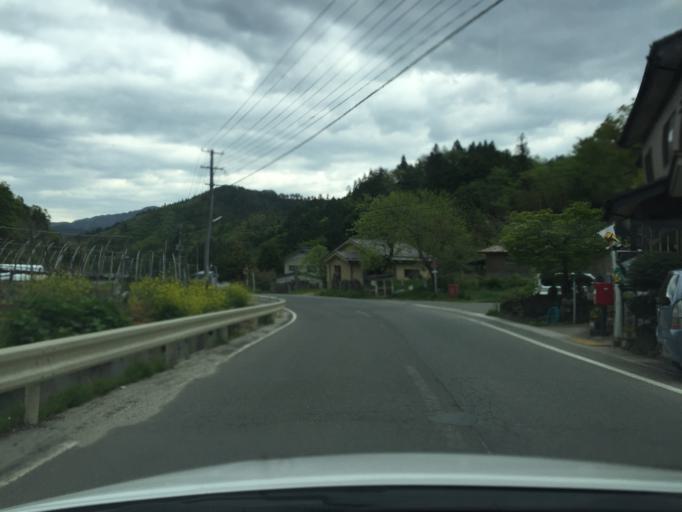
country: JP
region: Fukushima
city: Yanagawamachi-saiwaicho
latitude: 37.7493
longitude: 140.6402
